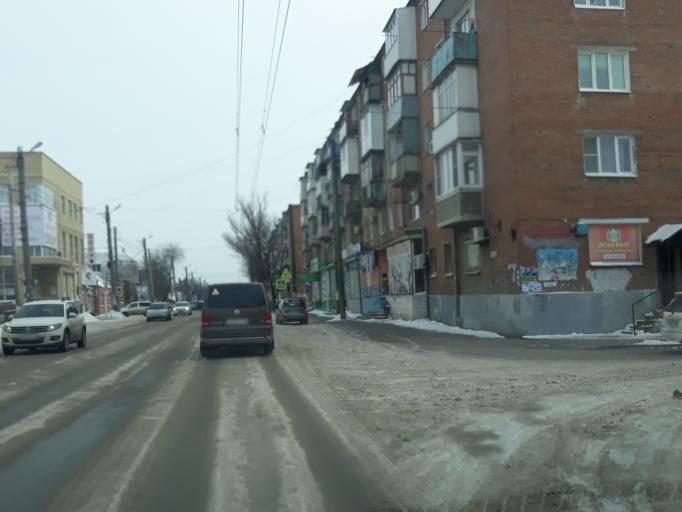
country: RU
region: Rostov
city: Taganrog
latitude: 47.2218
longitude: 38.8870
